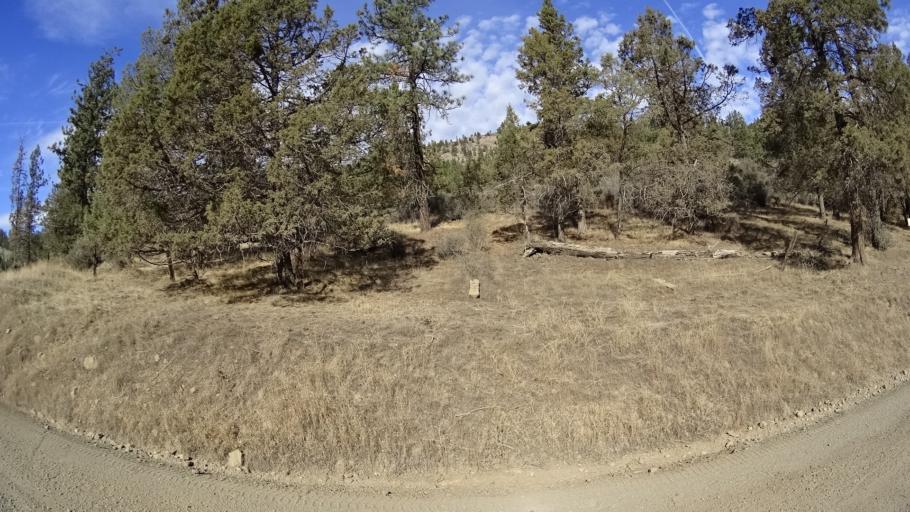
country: US
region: California
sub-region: Siskiyou County
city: Yreka
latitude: 41.6105
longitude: -122.7313
